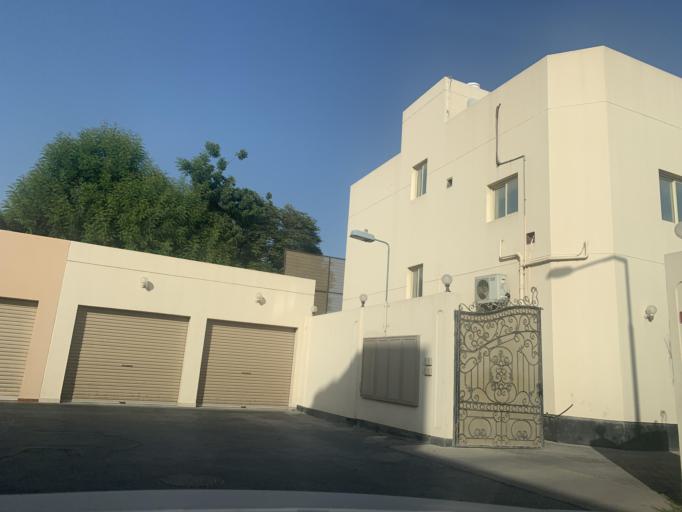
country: BH
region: Manama
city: Jidd Hafs
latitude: 26.1984
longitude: 50.4822
